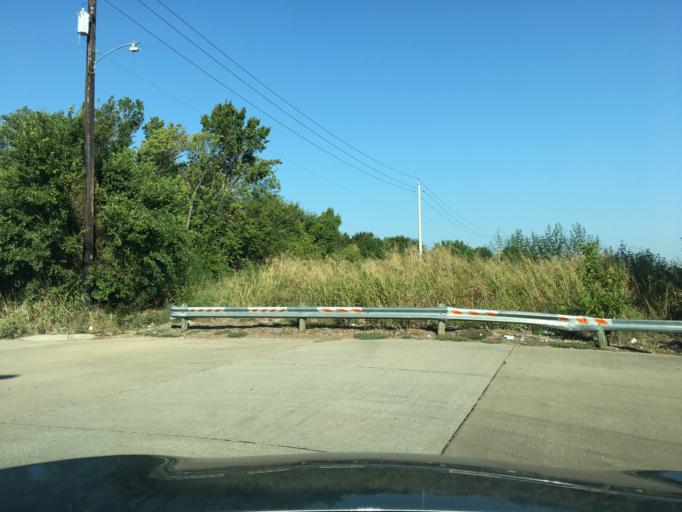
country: US
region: Texas
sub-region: Dallas County
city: Garland
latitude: 32.9643
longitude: -96.6496
